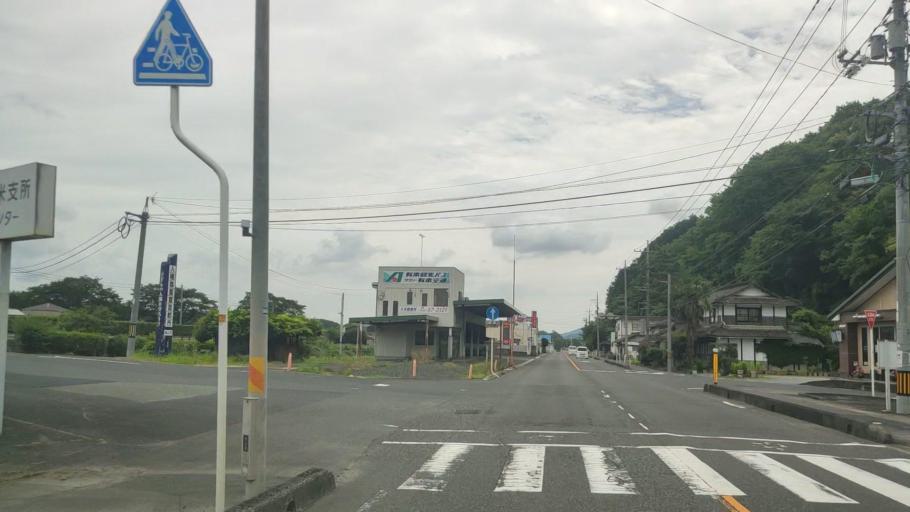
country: JP
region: Okayama
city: Tsuyama
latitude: 35.0587
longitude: 133.8994
